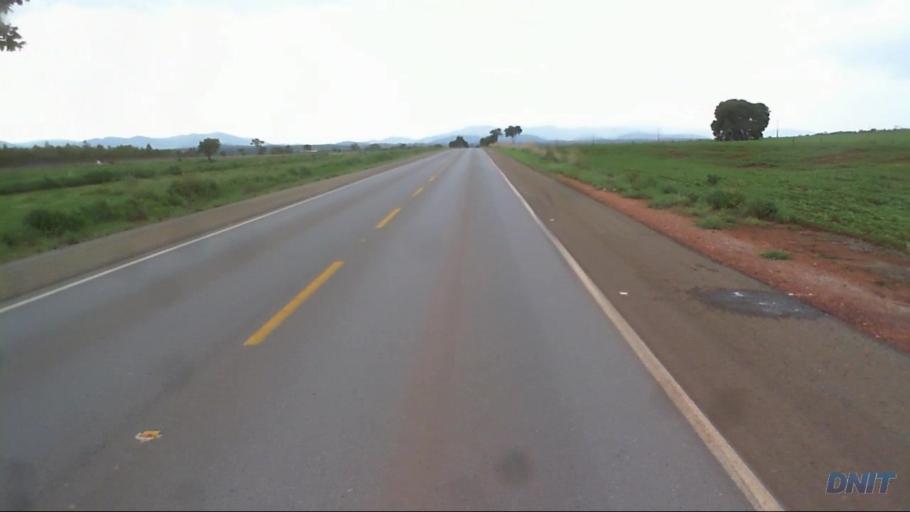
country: BR
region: Goias
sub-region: Barro Alto
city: Barro Alto
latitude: -14.7925
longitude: -49.0525
